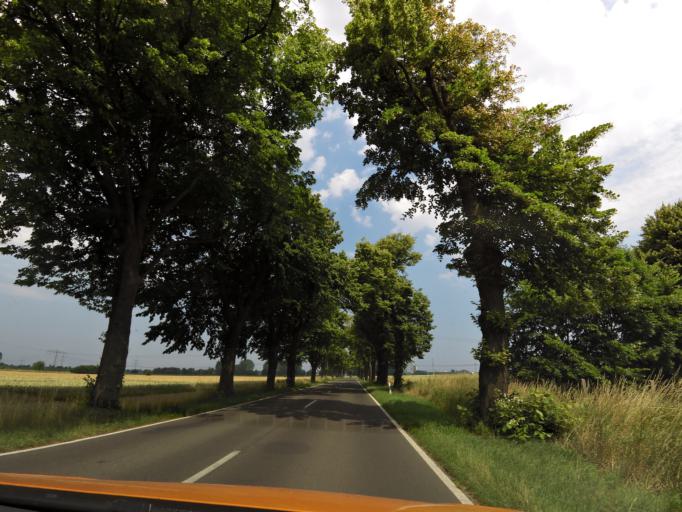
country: DE
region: Brandenburg
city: Nauen
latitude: 52.5833
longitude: 12.8754
